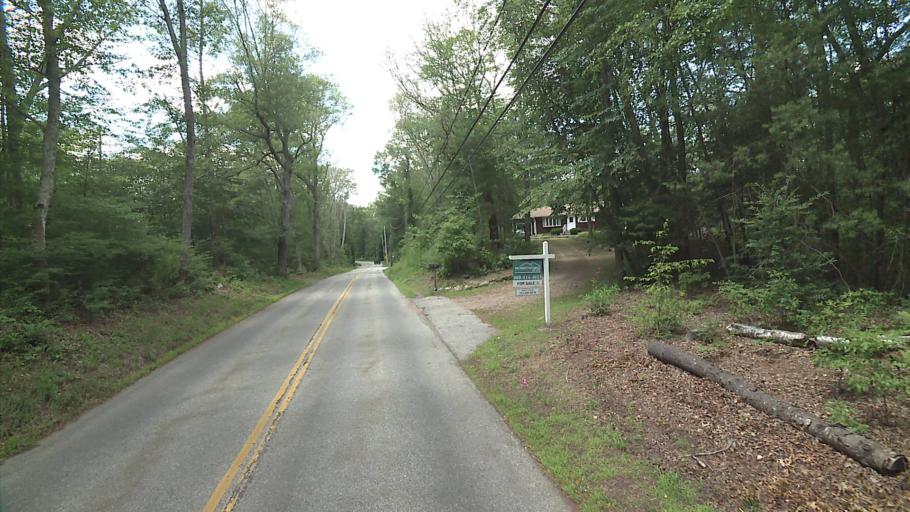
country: US
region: Connecticut
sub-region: New London County
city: Old Mystic
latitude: 41.4438
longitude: -71.8969
